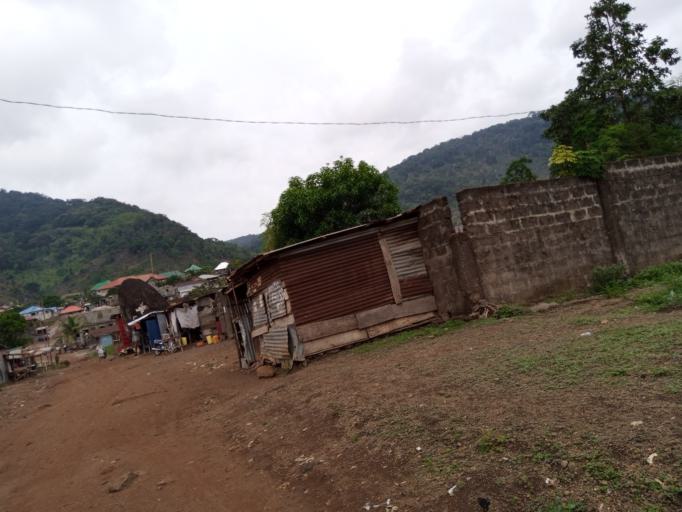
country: SL
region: Western Area
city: Hastings
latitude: 8.3775
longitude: -13.1538
